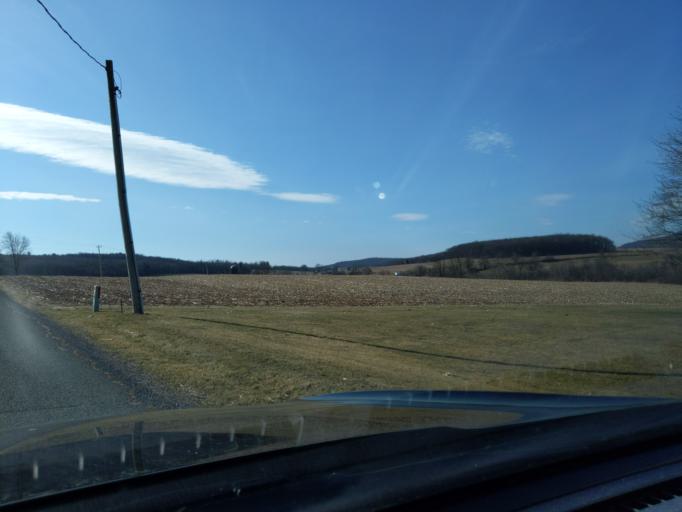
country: US
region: Pennsylvania
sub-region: Blair County
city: Martinsburg
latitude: 40.3927
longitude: -78.2740
